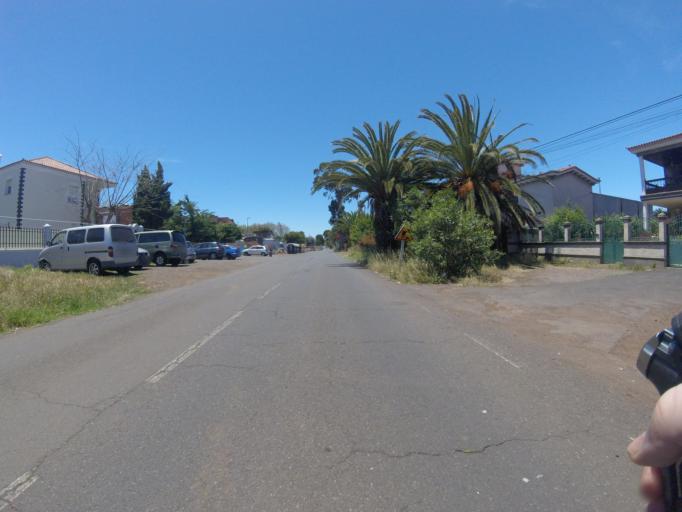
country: ES
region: Canary Islands
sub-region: Provincia de Santa Cruz de Tenerife
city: La Laguna
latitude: 28.4980
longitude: -16.3140
